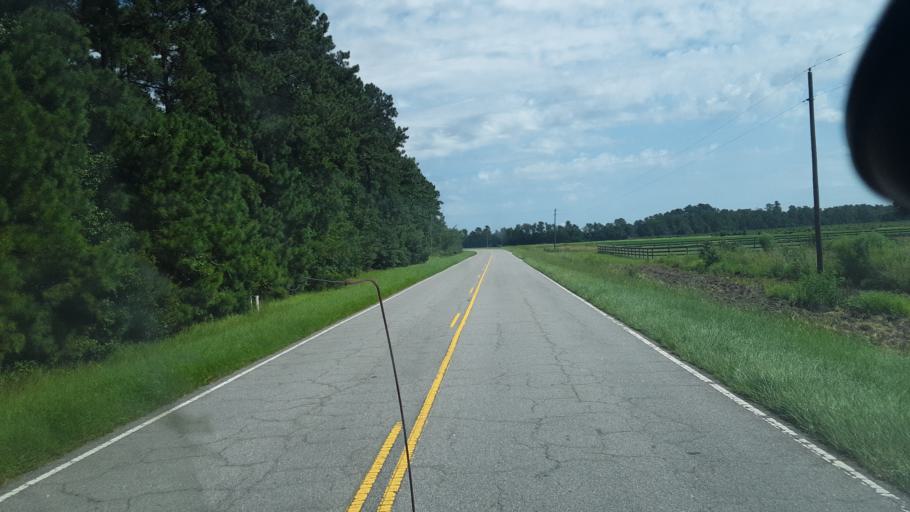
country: US
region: South Carolina
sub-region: Hampton County
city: Hampton
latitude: 33.0363
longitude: -81.0358
